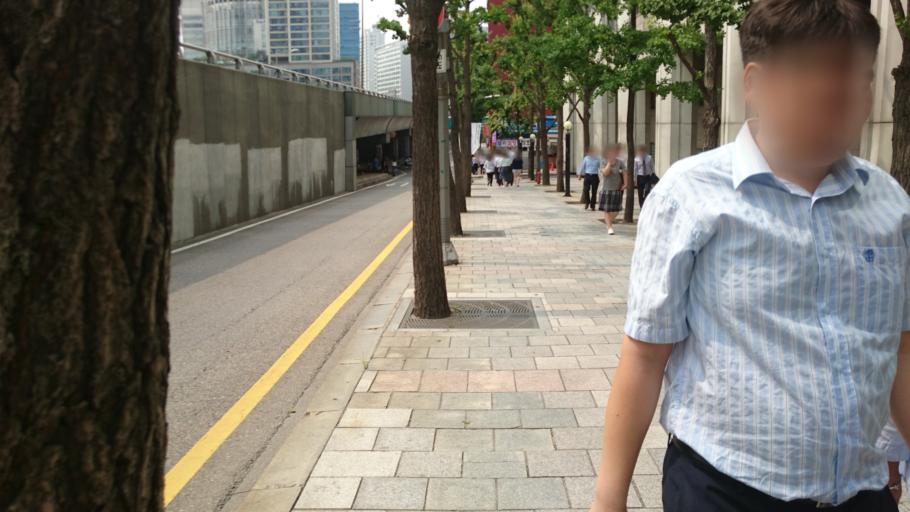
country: KR
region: Seoul
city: Seoul
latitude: 37.5619
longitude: 126.9714
